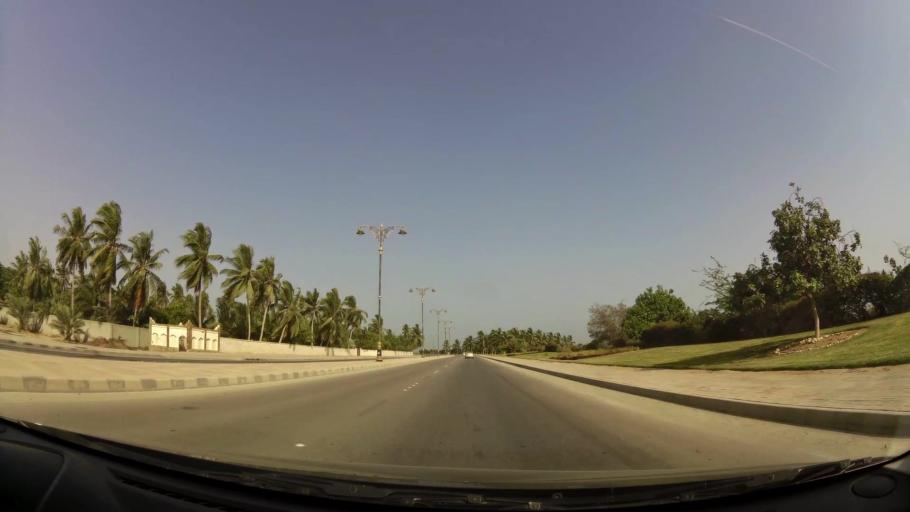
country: OM
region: Zufar
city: Salalah
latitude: 17.0003
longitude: 54.0695
